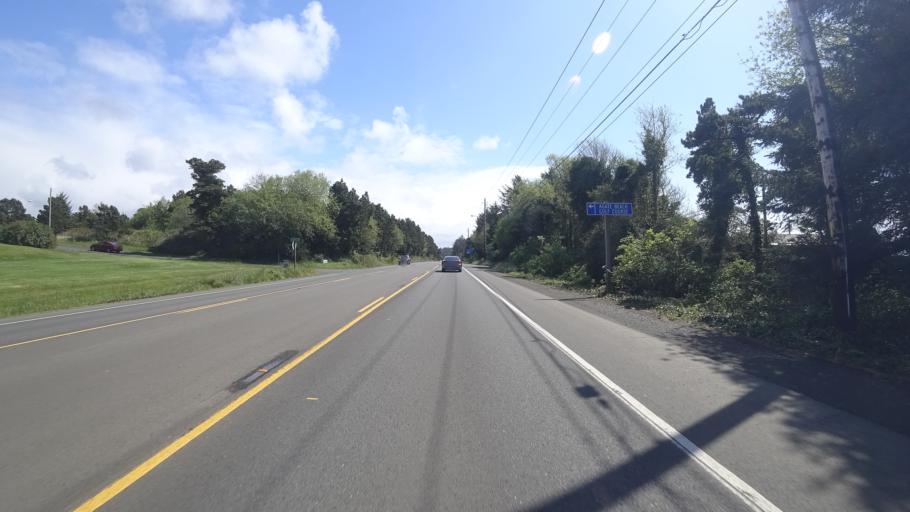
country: US
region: Oregon
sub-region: Lincoln County
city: Newport
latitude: 44.6674
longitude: -124.0571
